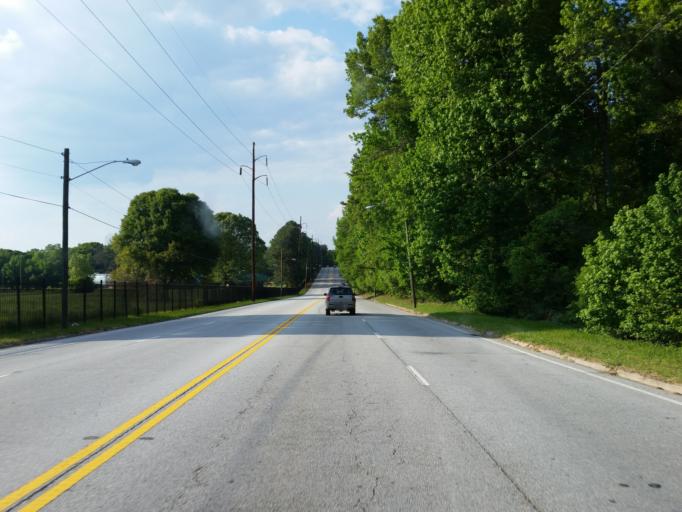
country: US
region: Georgia
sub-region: Cobb County
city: Vinings
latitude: 33.7820
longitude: -84.4766
